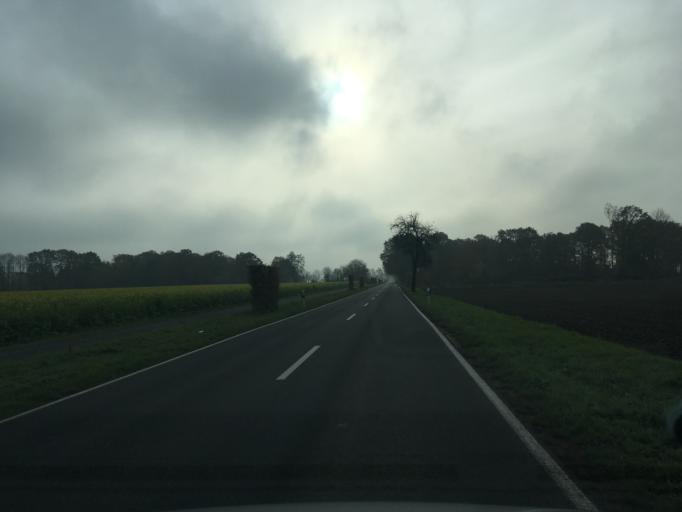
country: DE
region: North Rhine-Westphalia
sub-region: Regierungsbezirk Munster
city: Sudlohn
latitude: 51.9247
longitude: 6.9147
